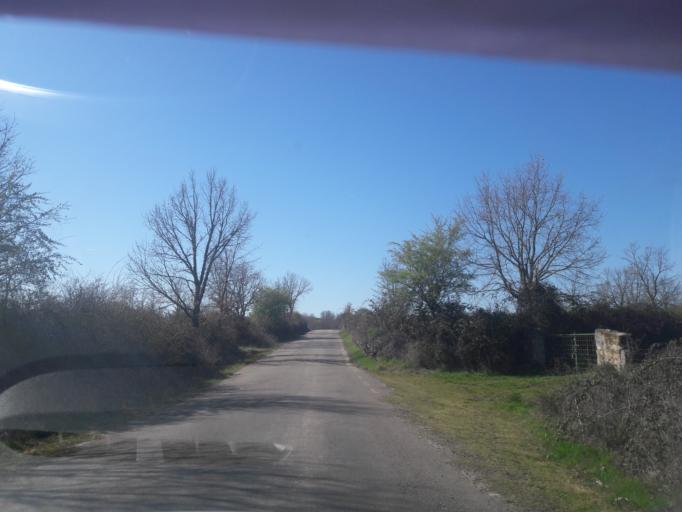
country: ES
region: Castille and Leon
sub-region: Provincia de Salamanca
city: Valsalabroso
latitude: 41.1467
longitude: -6.4863
